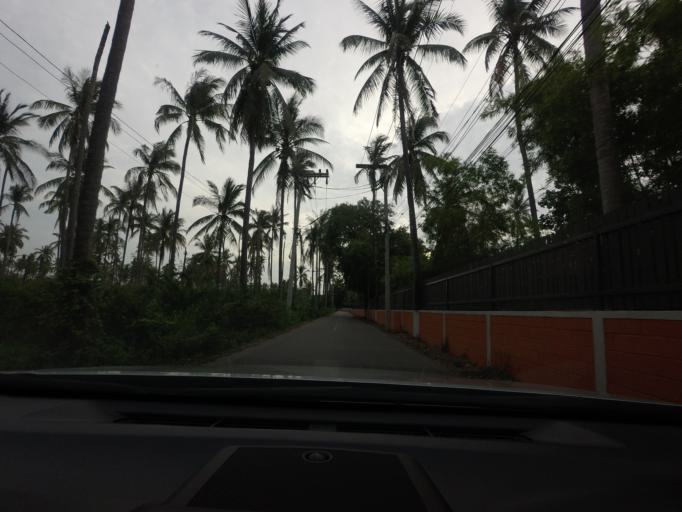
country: TH
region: Prachuap Khiri Khan
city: Pran Buri
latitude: 12.3839
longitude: 99.9984
